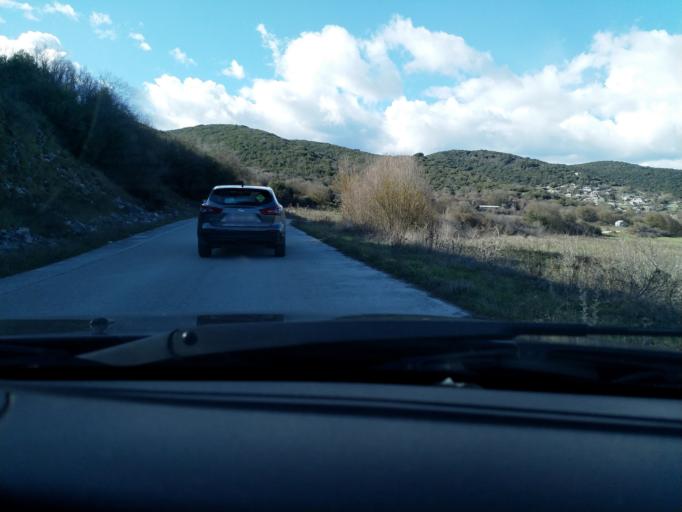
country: GR
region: Epirus
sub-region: Nomos Ioanninon
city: Kalpaki
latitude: 39.8758
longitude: 20.6857
